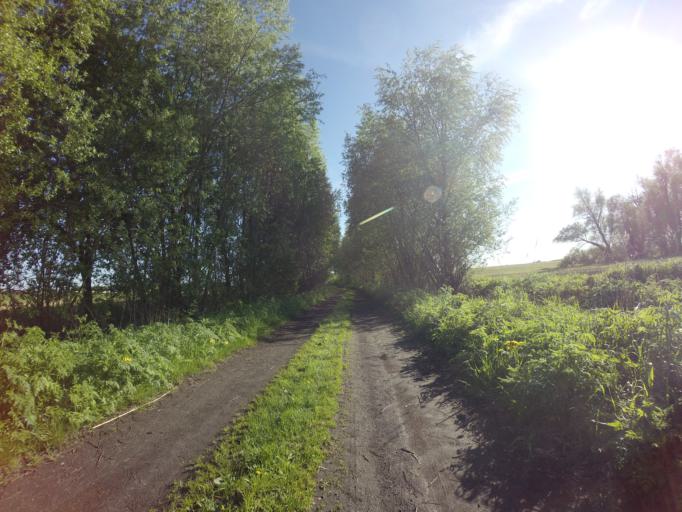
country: PL
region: West Pomeranian Voivodeship
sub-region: Powiat choszczenski
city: Pelczyce
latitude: 53.1259
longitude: 15.3239
